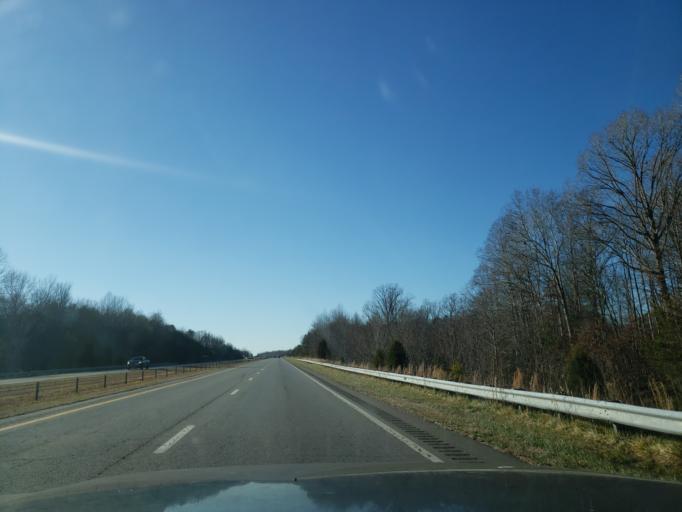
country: US
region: North Carolina
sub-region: Yadkin County
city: Yadkinville
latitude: 36.1197
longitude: -80.6832
